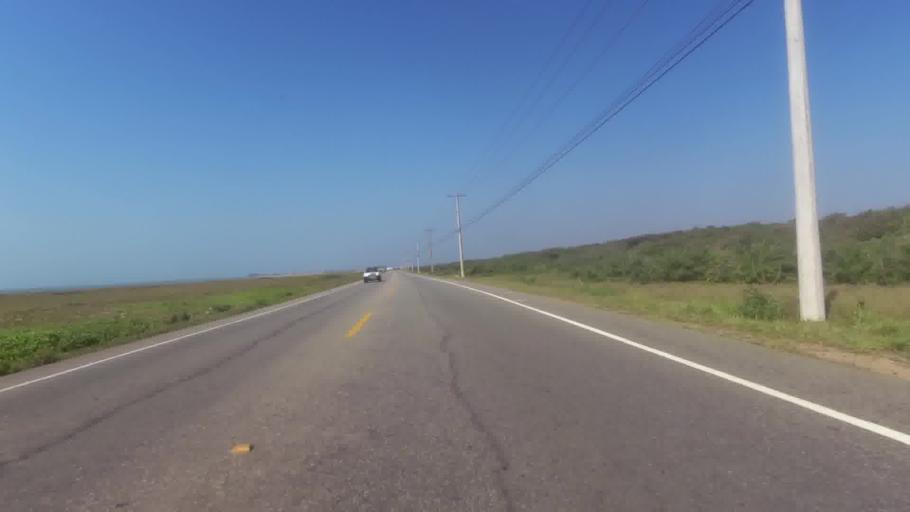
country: BR
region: Espirito Santo
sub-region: Itapemirim
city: Itapemirim
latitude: -20.9713
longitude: -40.8113
